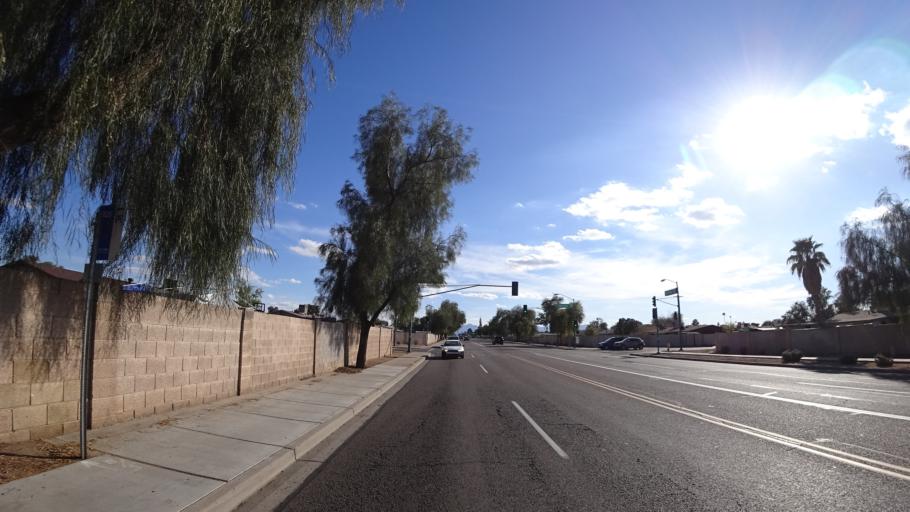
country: US
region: Arizona
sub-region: Maricopa County
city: Tolleson
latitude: 33.4982
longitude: -112.2377
